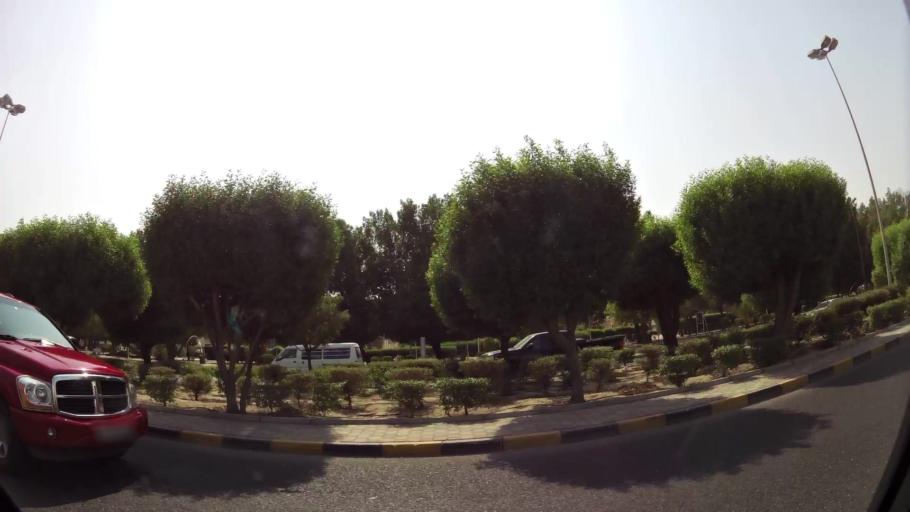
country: KW
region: Al Asimah
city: Ash Shamiyah
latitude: 29.3337
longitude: 47.9570
